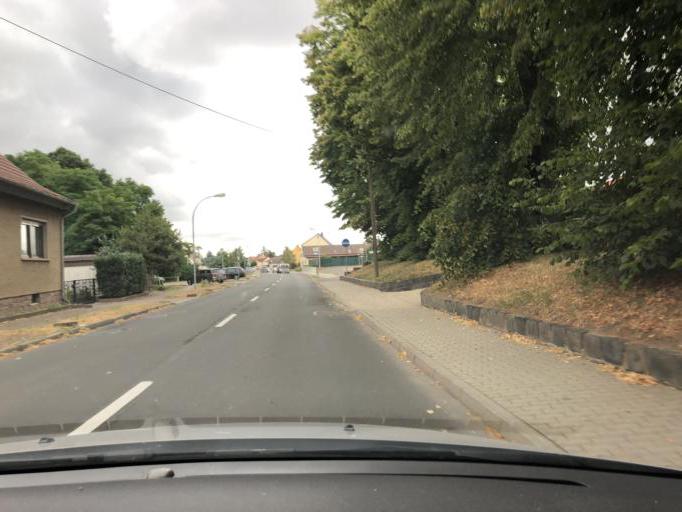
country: DE
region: Saxony-Anhalt
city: Rassnitz
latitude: 51.3933
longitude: 12.1045
